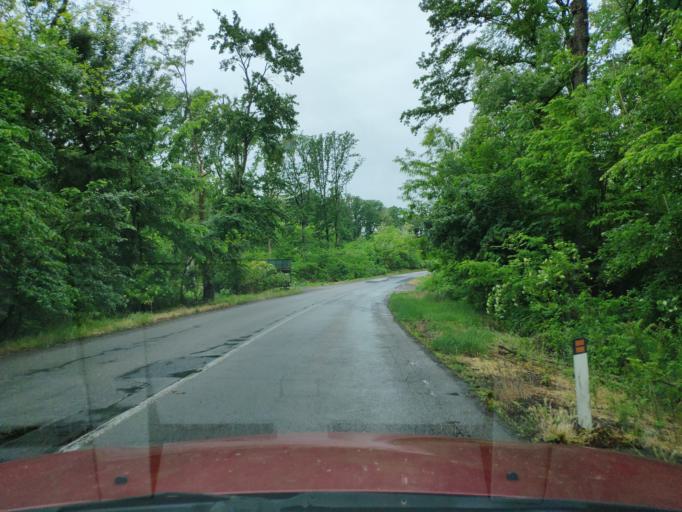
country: HU
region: Borsod-Abauj-Zemplen
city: Ricse
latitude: 48.4350
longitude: 21.9536
